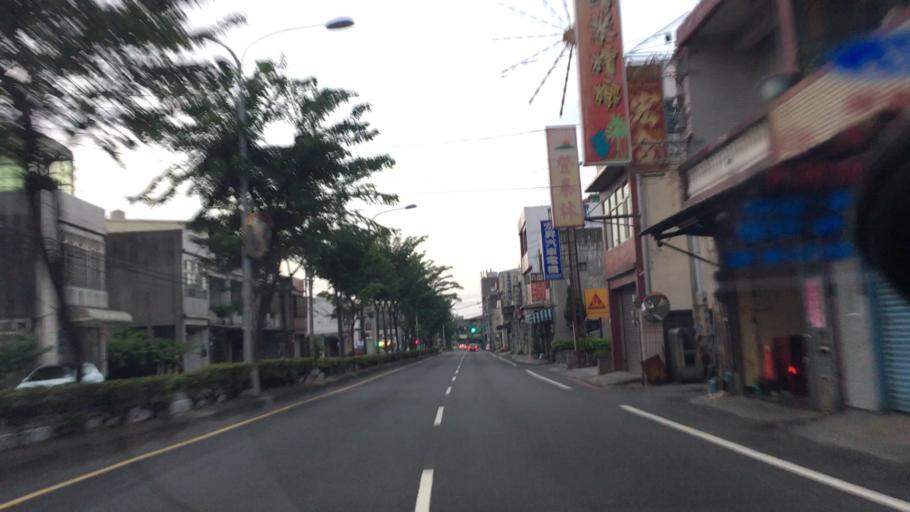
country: TW
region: Taiwan
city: Taoyuan City
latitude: 25.0600
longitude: 121.2673
